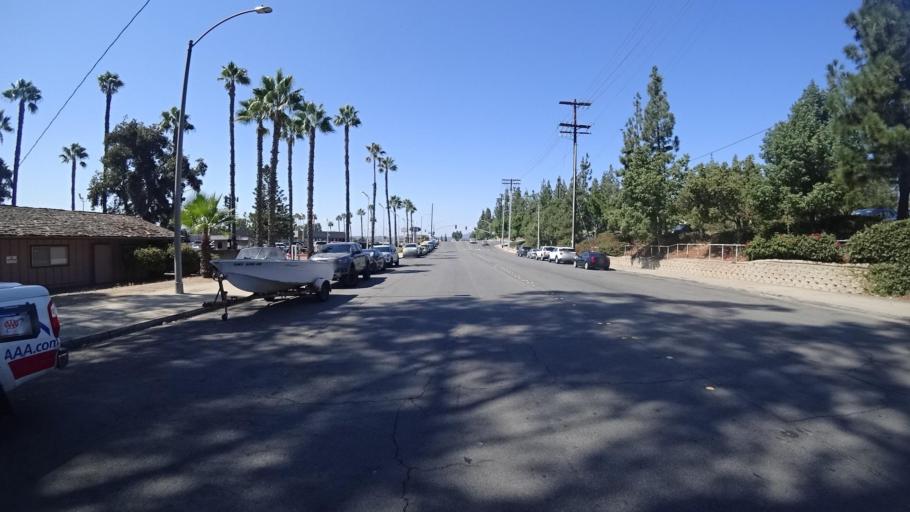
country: US
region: California
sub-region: San Diego County
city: Bostonia
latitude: 32.8077
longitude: -116.9203
